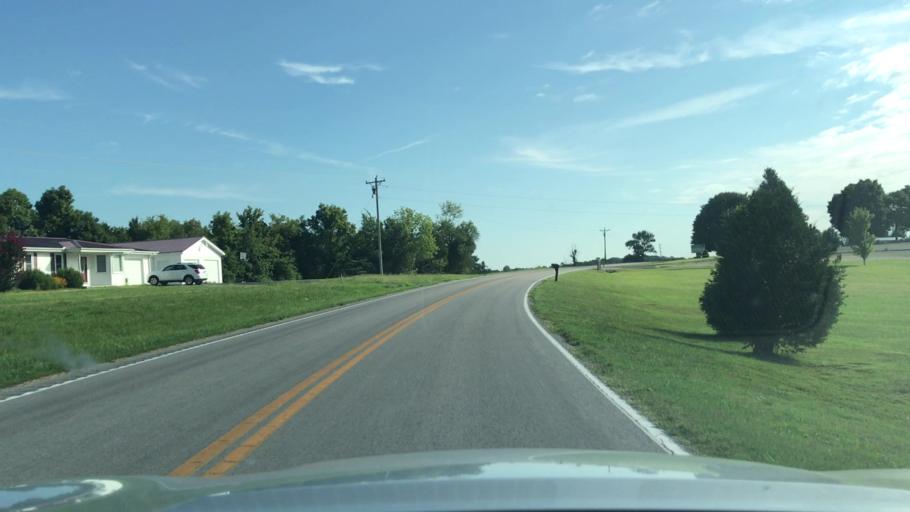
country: US
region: Kentucky
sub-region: Todd County
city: Elkton
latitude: 36.9313
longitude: -87.1616
